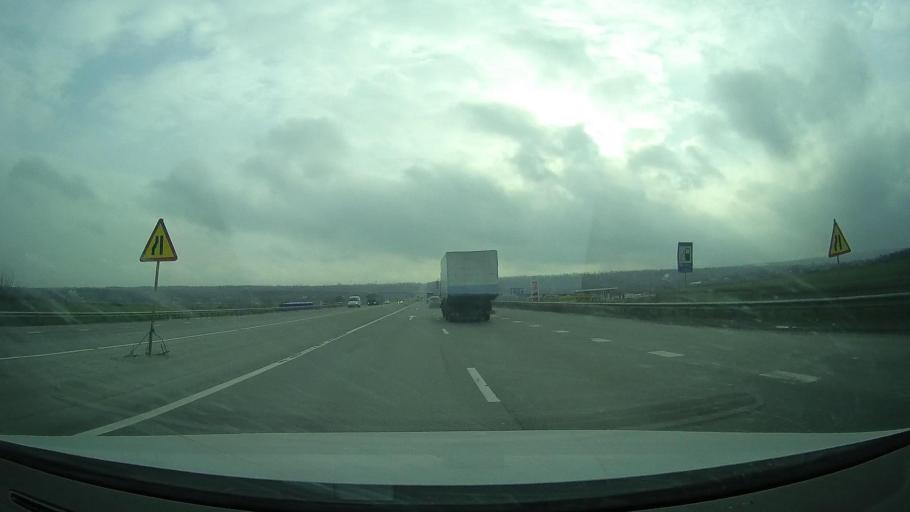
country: RU
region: Rostov
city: Grushevskaya
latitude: 47.4498
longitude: 39.9741
